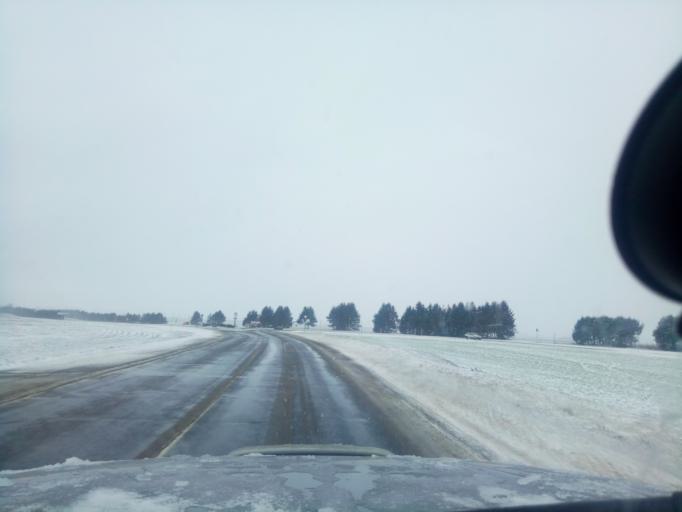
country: BY
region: Minsk
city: Haradzyeya
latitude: 53.2952
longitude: 26.5751
